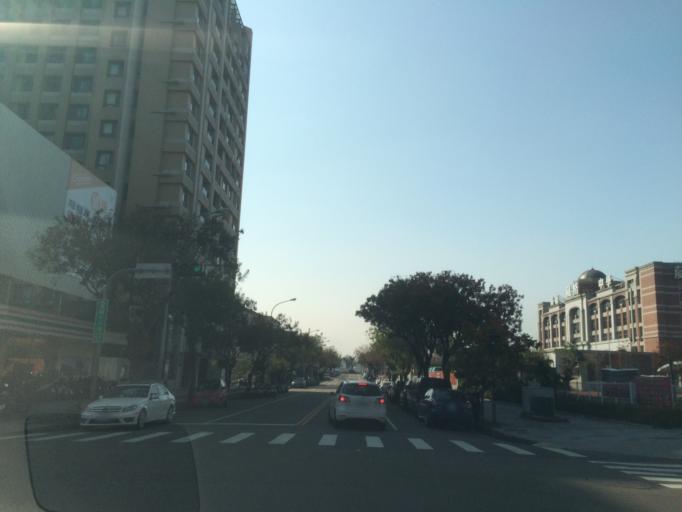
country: TW
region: Taiwan
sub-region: Taichung City
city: Taichung
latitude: 24.1782
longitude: 120.7134
